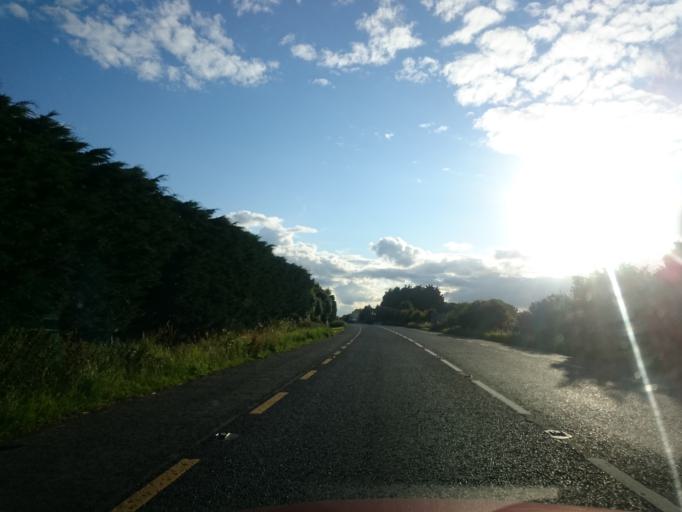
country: IE
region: Leinster
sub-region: Loch Garman
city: Ballygerry
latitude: 52.2447
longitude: -6.3748
